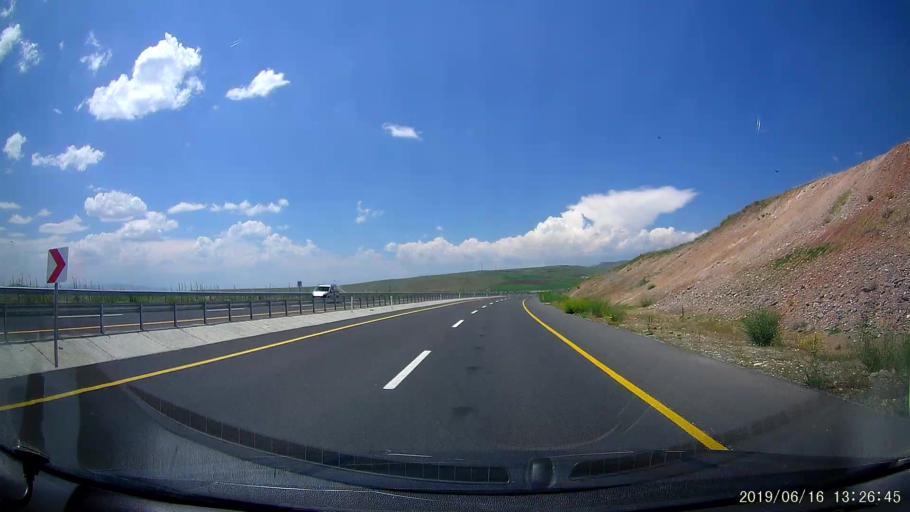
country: TR
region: Agri
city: Taslicay
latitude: 39.6613
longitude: 43.3210
